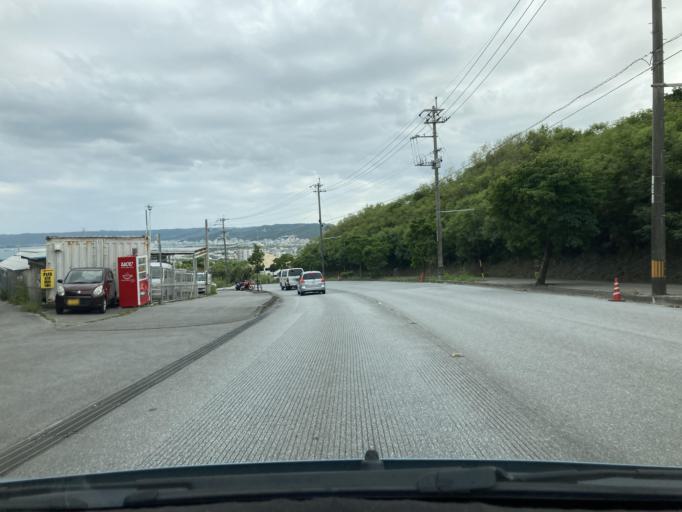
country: JP
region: Okinawa
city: Ginowan
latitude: 26.2359
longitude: 127.7663
